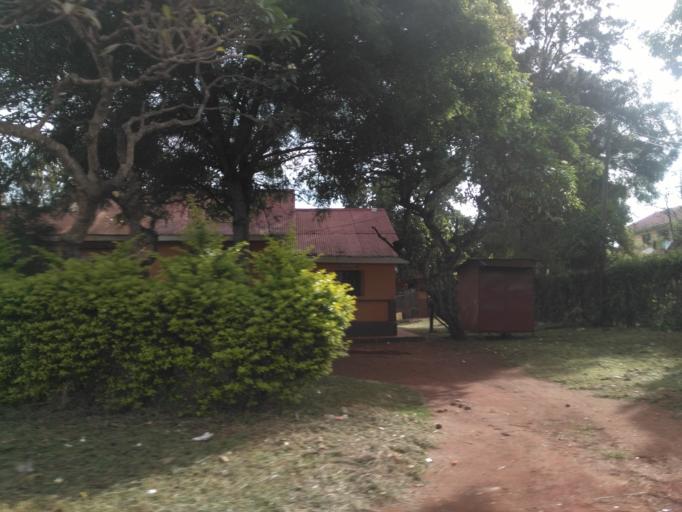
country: UG
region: Eastern Region
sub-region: Jinja District
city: Jinja
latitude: 0.4265
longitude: 33.2058
